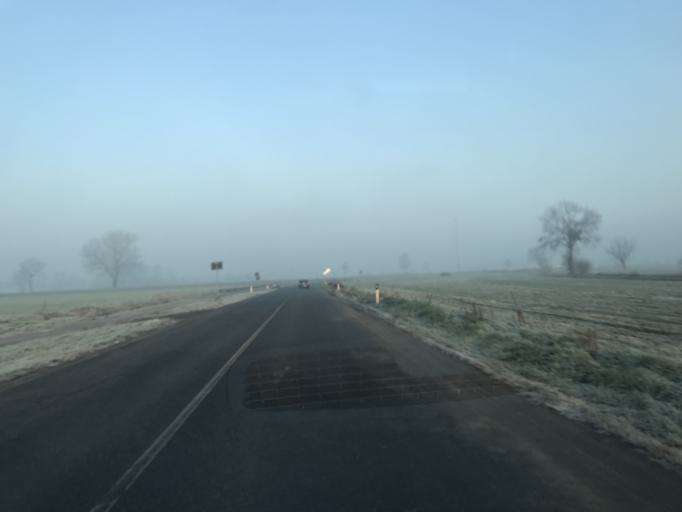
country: IT
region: Lombardy
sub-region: Provincia di Lodi
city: Bargano
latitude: 45.2544
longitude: 9.4337
